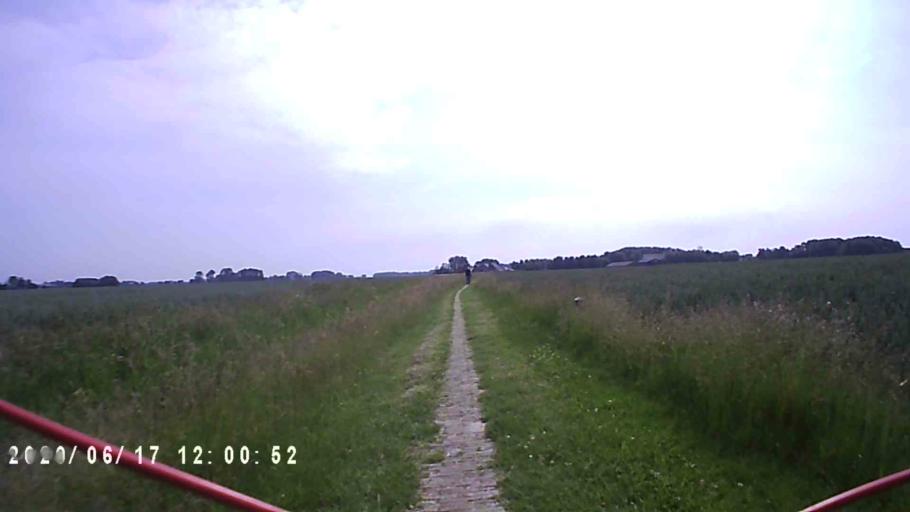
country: NL
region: Groningen
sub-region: Gemeente De Marne
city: Ulrum
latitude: 53.3416
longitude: 6.3330
